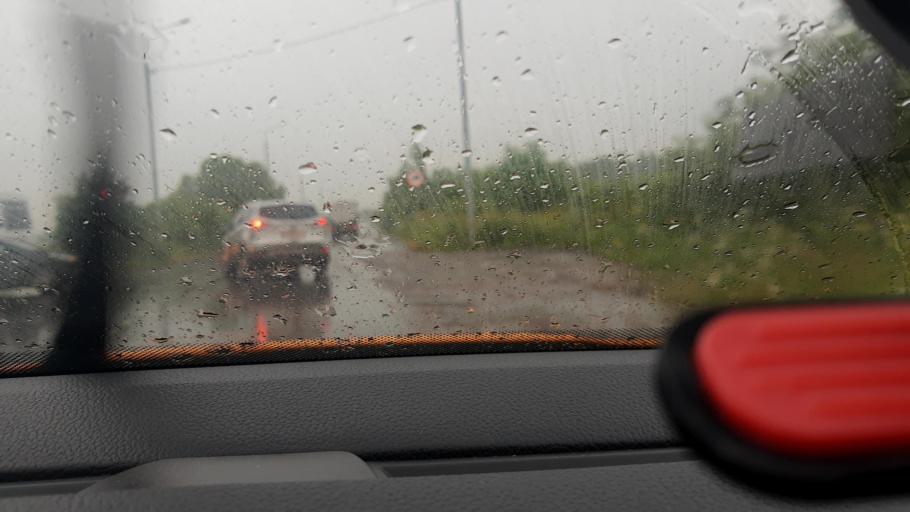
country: RU
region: Moskovskaya
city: Novopodrezkovo
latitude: 55.9349
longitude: 37.3805
